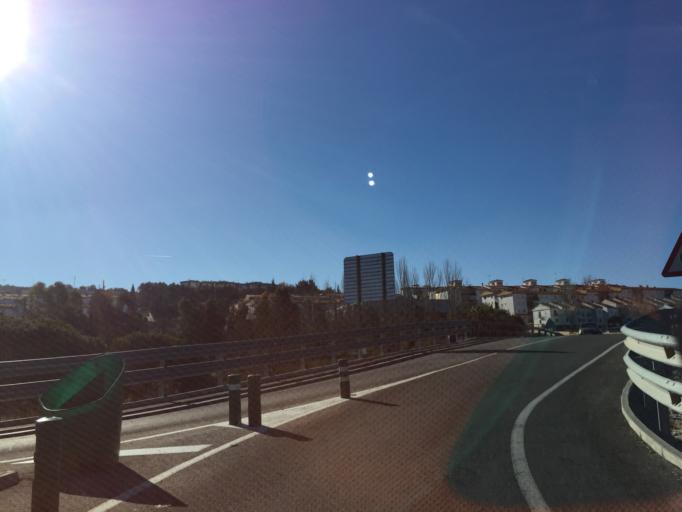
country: ES
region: Andalusia
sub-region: Provincia de Malaga
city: Ronda
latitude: 36.7553
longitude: -5.1725
